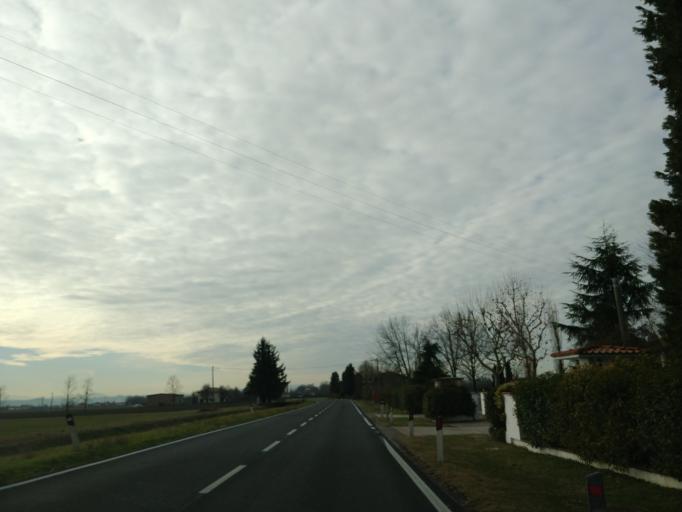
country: IT
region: Emilia-Romagna
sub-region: Provincia di Bologna
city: Argelato
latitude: 44.6287
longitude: 11.3406
